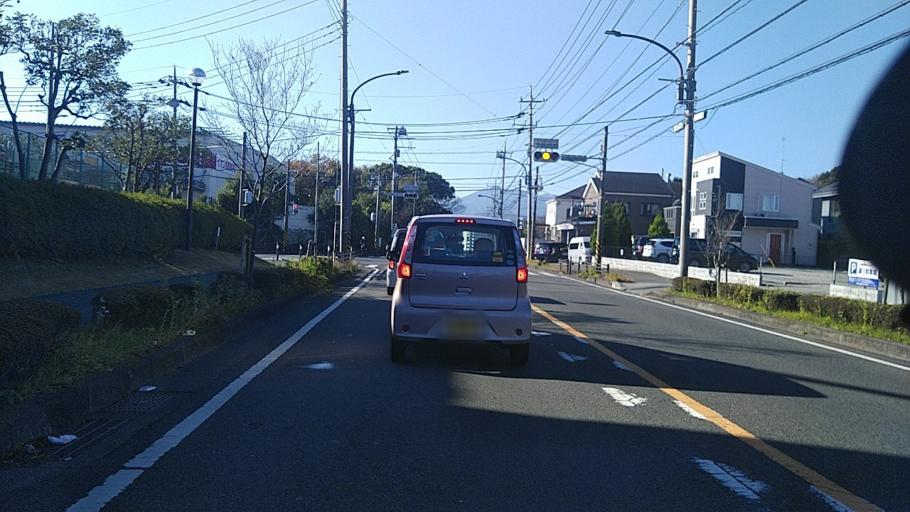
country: JP
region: Kanagawa
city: Zama
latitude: 35.5380
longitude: 139.3572
